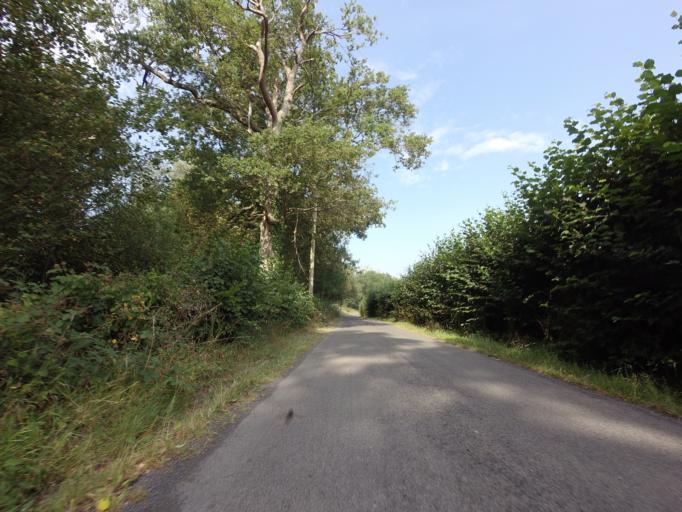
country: GB
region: England
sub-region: Kent
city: Headcorn
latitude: 51.1209
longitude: 0.6016
